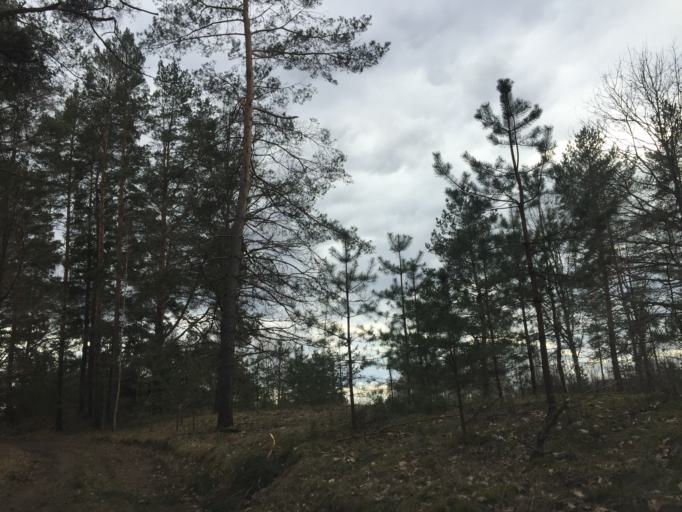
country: LV
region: Lielvarde
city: Lielvarde
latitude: 56.4904
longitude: 24.7799
